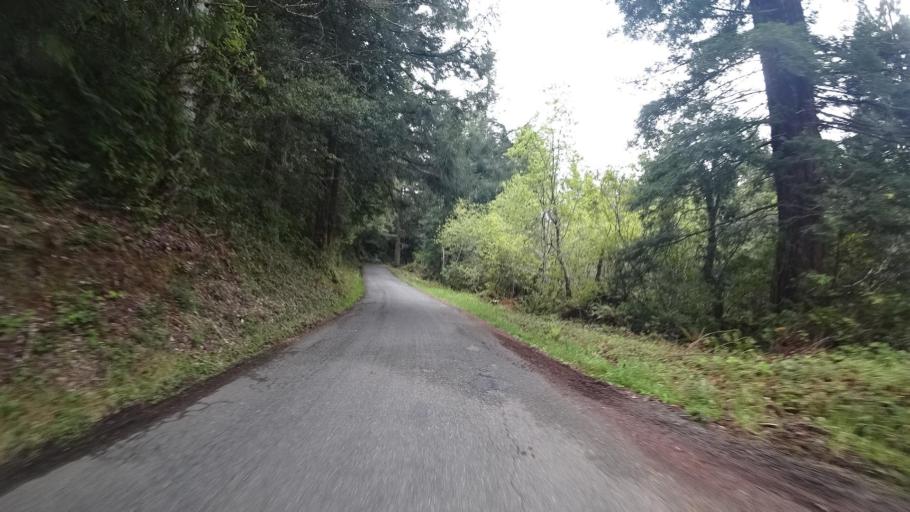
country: US
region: California
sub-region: Humboldt County
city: Blue Lake
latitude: 40.8243
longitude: -124.0006
